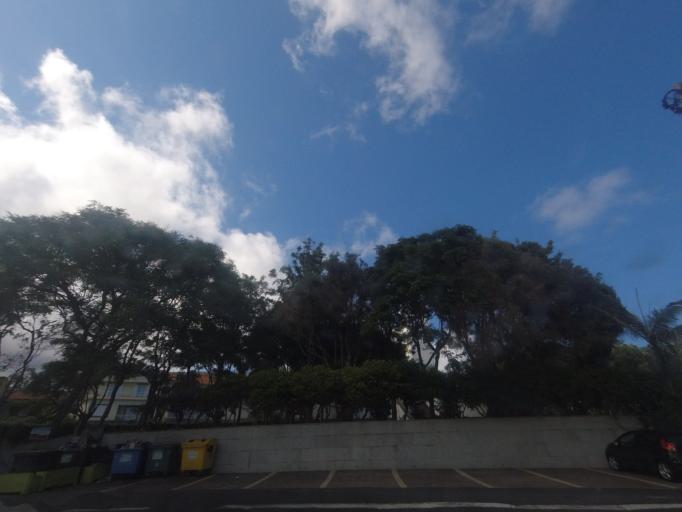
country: PT
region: Madeira
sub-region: Machico
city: Canical
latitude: 32.7384
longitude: -16.7363
